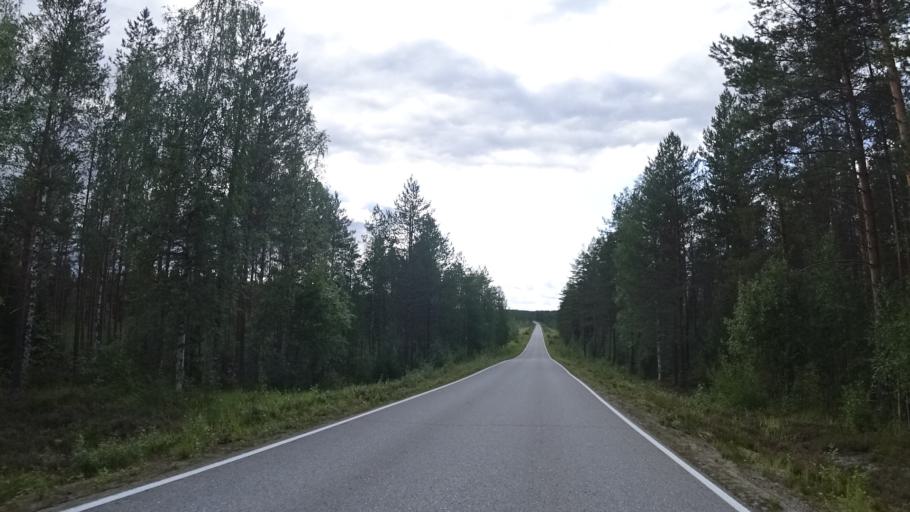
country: FI
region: North Karelia
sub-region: Joensuu
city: Ilomantsi
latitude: 62.4398
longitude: 31.0797
